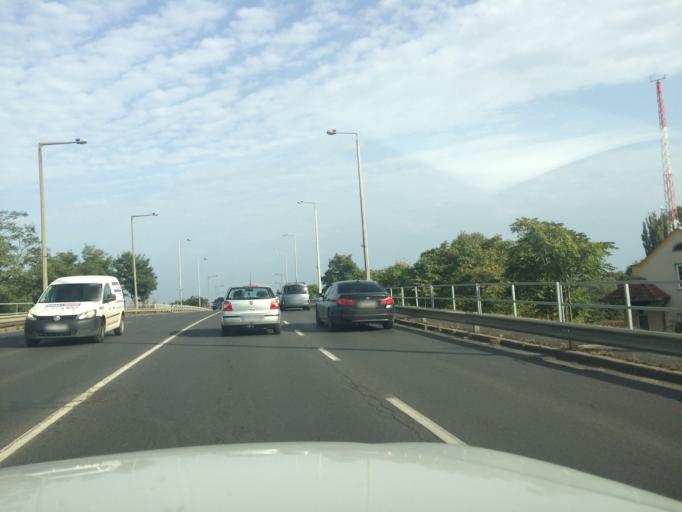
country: HU
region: Szabolcs-Szatmar-Bereg
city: Nyiregyhaza
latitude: 47.9399
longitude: 21.7190
